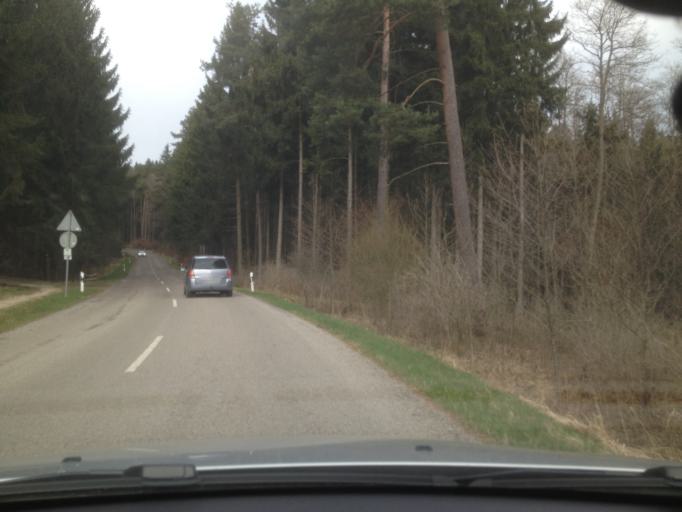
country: DE
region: Bavaria
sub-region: Swabia
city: Wehringen
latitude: 48.2777
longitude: 10.7813
